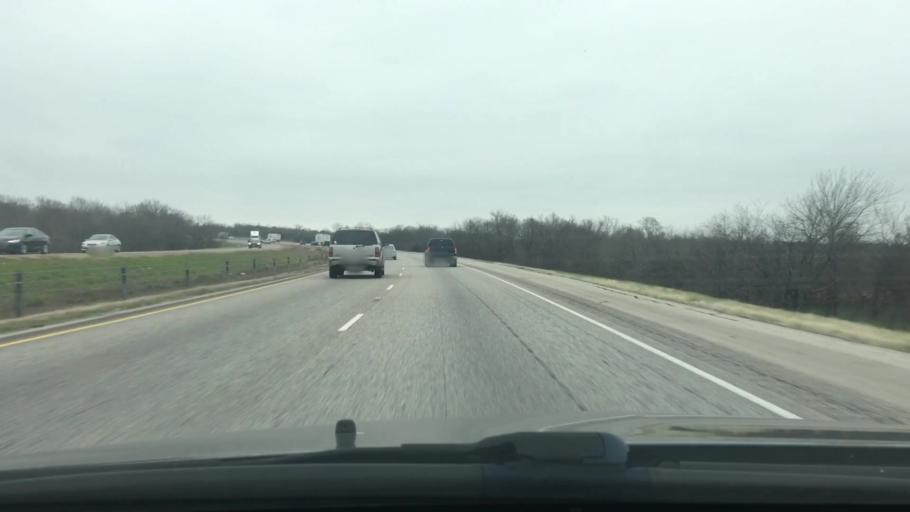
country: US
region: Texas
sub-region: Freestone County
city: Wortham
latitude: 31.8711
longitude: -96.3373
